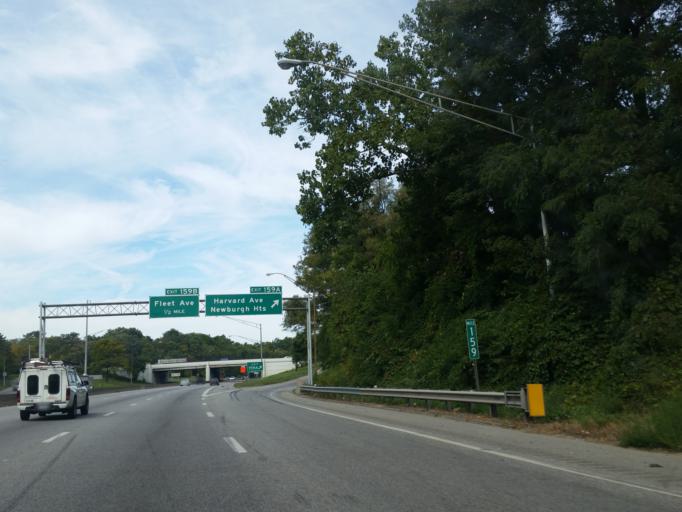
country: US
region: Ohio
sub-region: Cuyahoga County
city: Newburgh Heights
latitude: 41.4458
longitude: -81.6538
